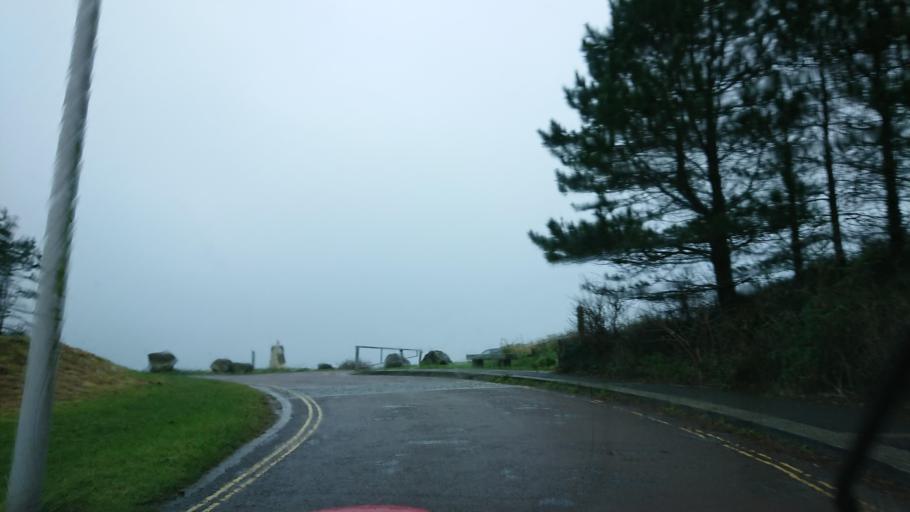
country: GB
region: England
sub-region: Plymouth
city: Plymouth
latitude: 50.3593
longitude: -4.1289
